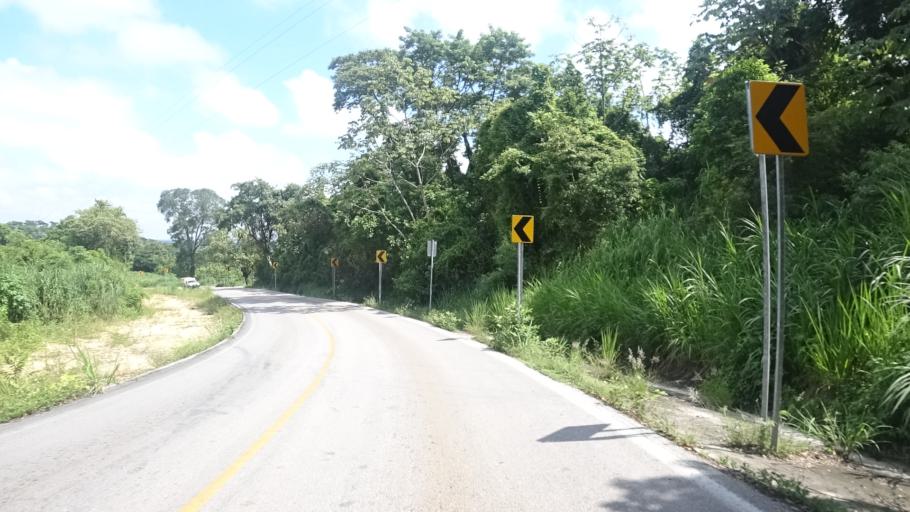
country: MX
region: Chiapas
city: Palenque
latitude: 17.4759
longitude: -91.9658
